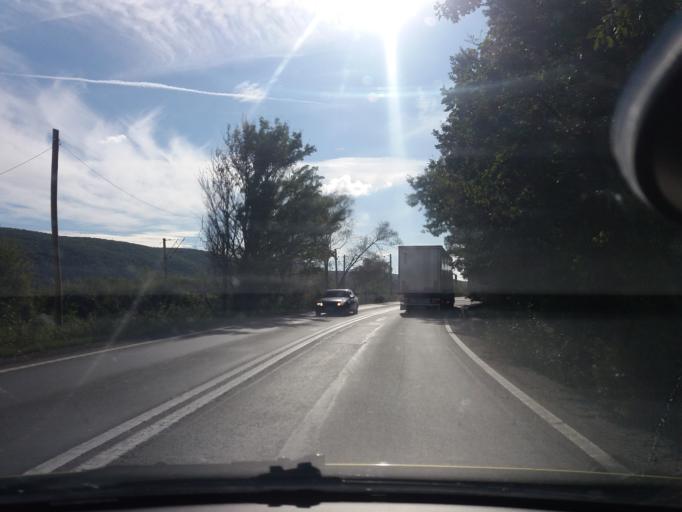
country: RO
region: Arad
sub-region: Comuna Petris
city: Petris
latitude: 46.0049
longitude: 22.3381
